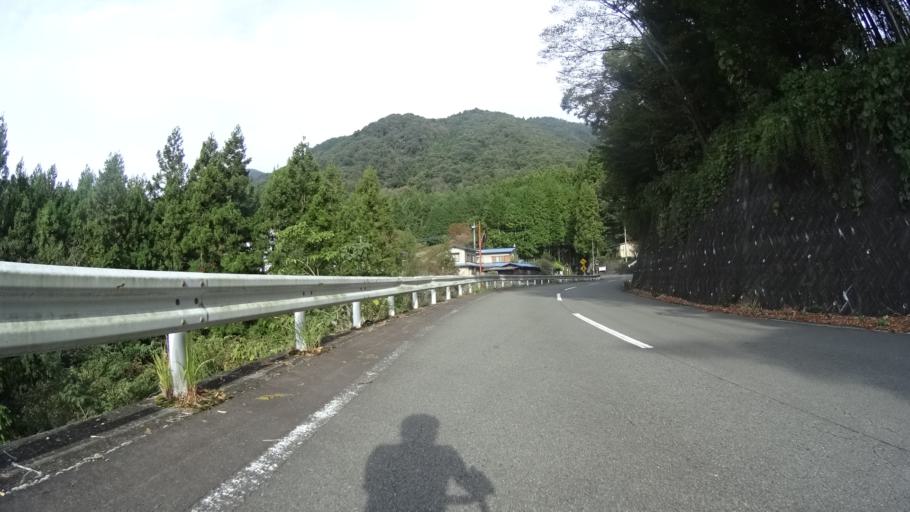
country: JP
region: Yamanashi
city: Uenohara
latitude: 35.6275
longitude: 139.0390
